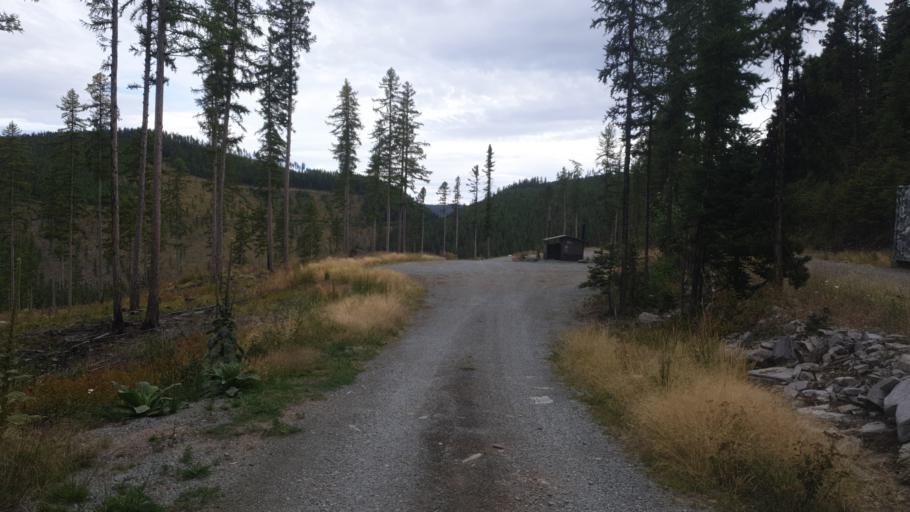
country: US
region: Montana
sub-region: Flathead County
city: Lakeside
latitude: 47.9876
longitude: -114.3223
